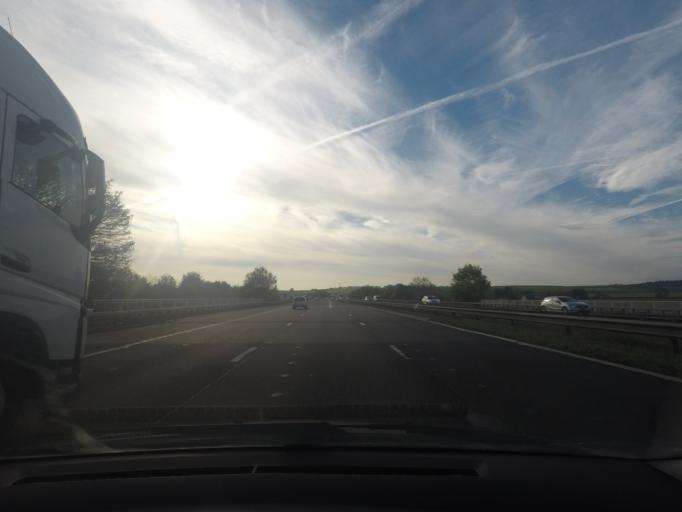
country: GB
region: England
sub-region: Barnsley
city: Darton
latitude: 53.6027
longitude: -1.5506
